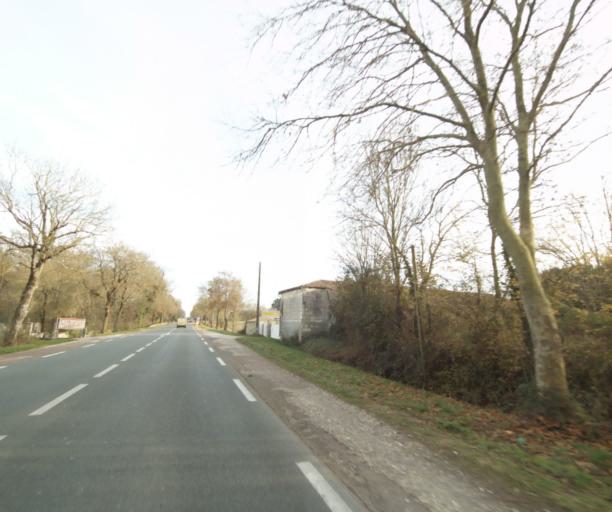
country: FR
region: Poitou-Charentes
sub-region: Departement de la Charente-Maritime
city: Saint-Georges-des-Coteaux
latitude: 45.7757
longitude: -0.6968
